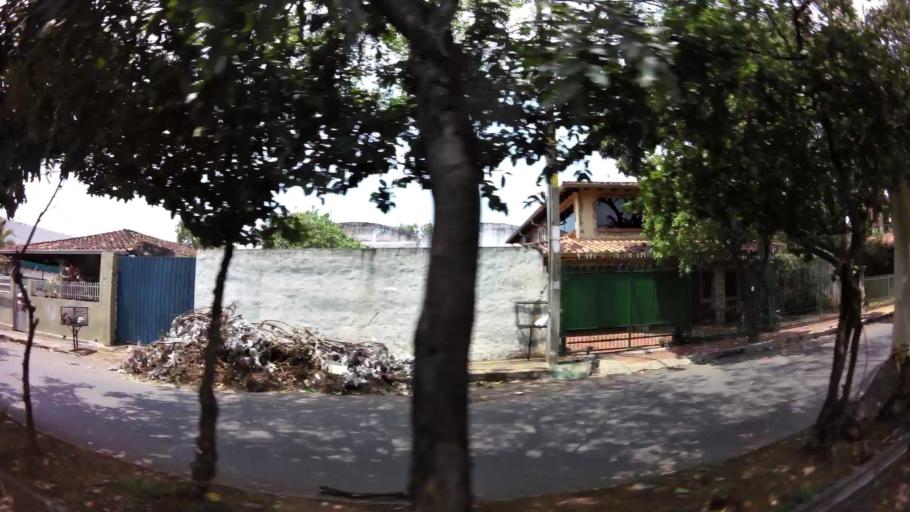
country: PY
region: Central
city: Fernando de la Mora
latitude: -25.3080
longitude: -57.5671
